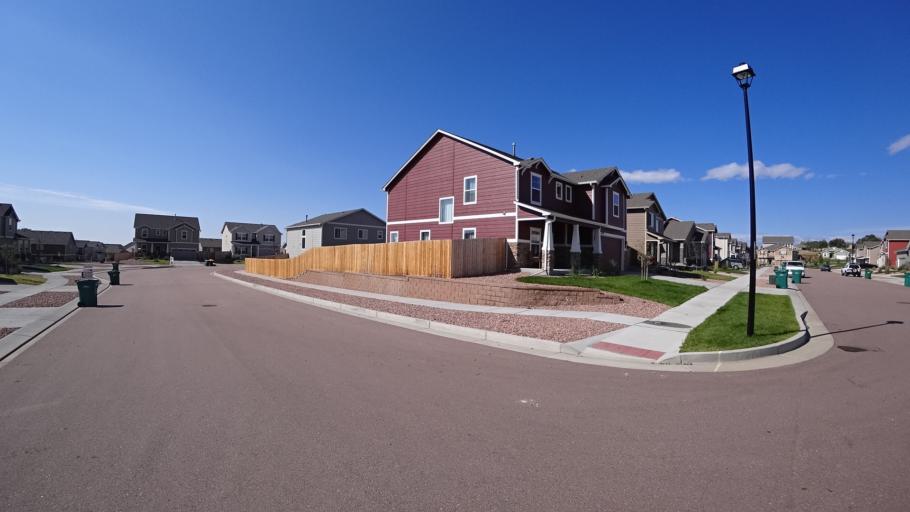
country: US
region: Colorado
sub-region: El Paso County
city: Cimarron Hills
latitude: 38.9343
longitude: -104.6937
